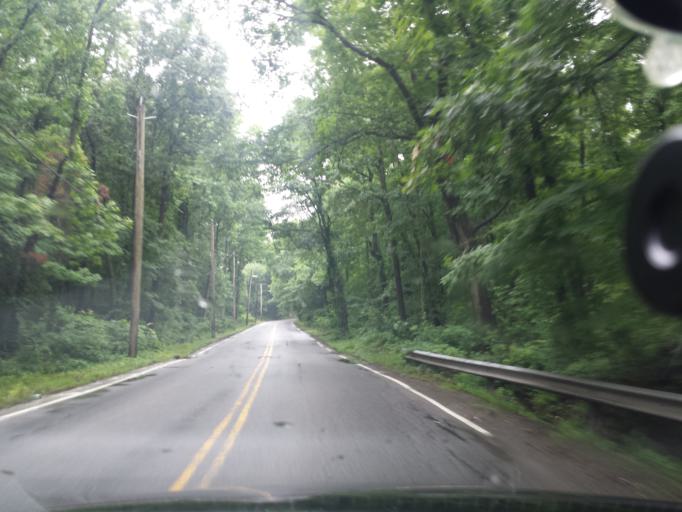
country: US
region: New York
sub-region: Richmond County
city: Staten Island
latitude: 40.5931
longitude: -74.1264
